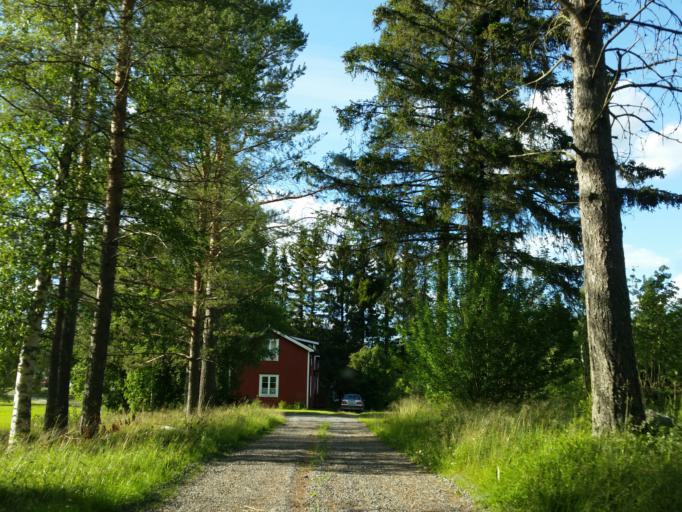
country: SE
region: Vaesterbotten
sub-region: Robertsfors Kommun
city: Robertsfors
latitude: 64.0396
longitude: 20.8618
